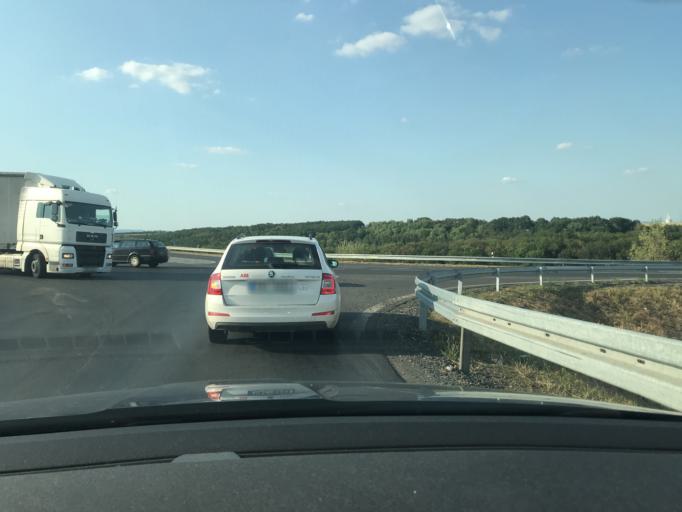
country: CZ
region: Ustecky
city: Postoloprty
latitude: 50.3709
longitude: 13.6316
